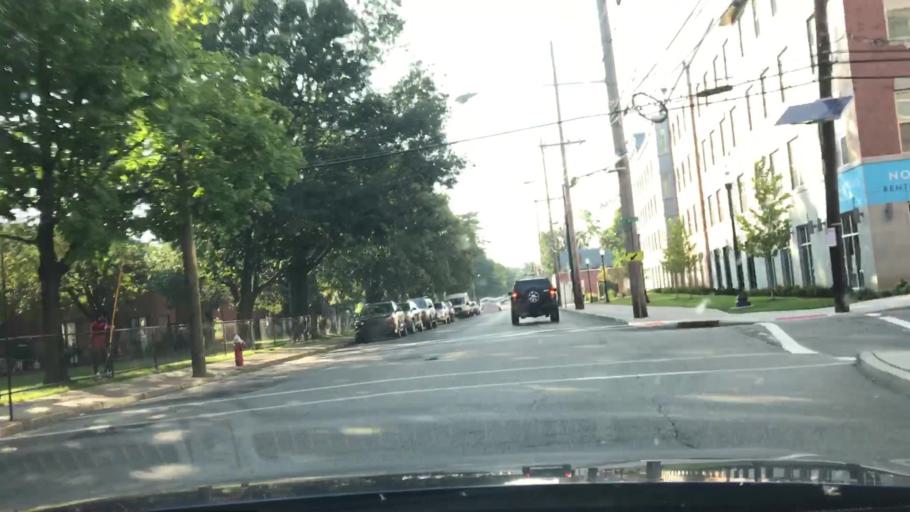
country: US
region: New Jersey
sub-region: Bergen County
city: Englewood
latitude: 40.8934
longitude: -73.9775
